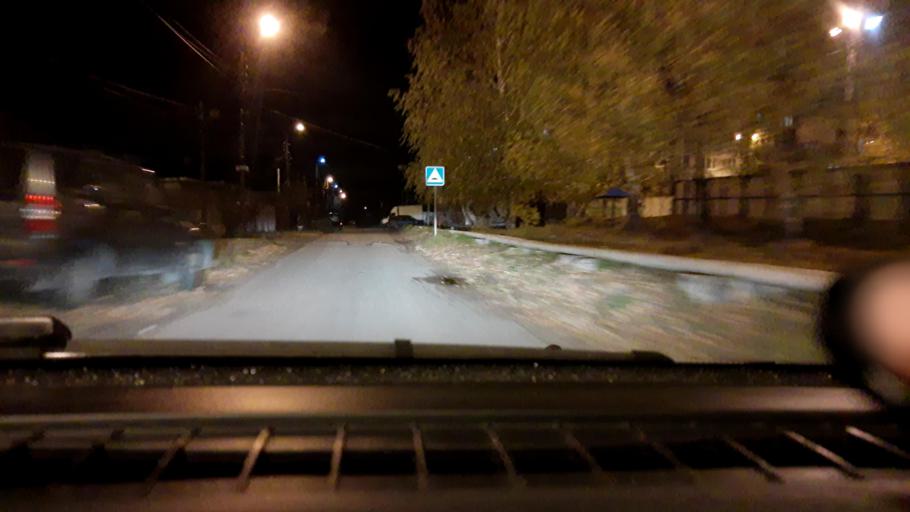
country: RU
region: Nizjnij Novgorod
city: Kstovo
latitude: 56.1667
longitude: 44.1974
